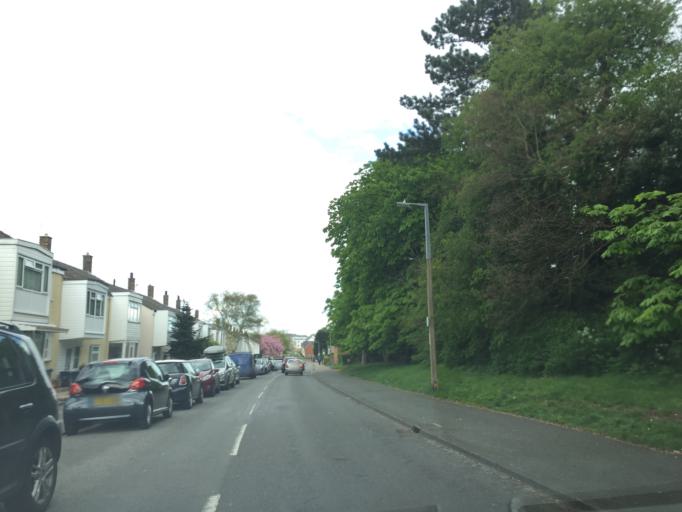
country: GB
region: England
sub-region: Essex
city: Harlow
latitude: 51.7754
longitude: 0.0863
